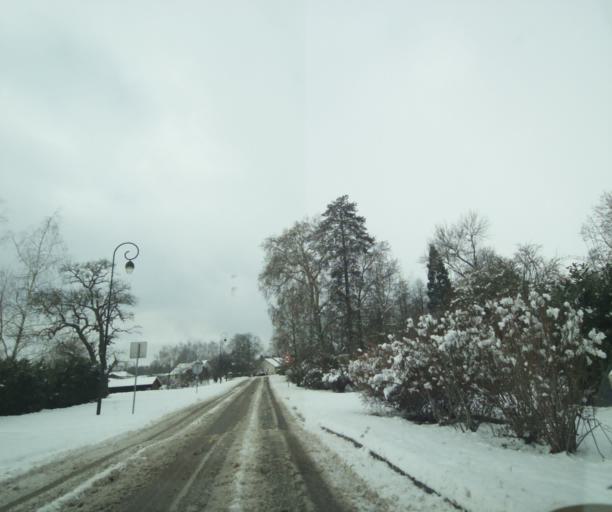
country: FR
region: Champagne-Ardenne
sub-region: Departement de la Haute-Marne
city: Montier-en-Der
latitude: 48.5109
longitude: 4.6981
